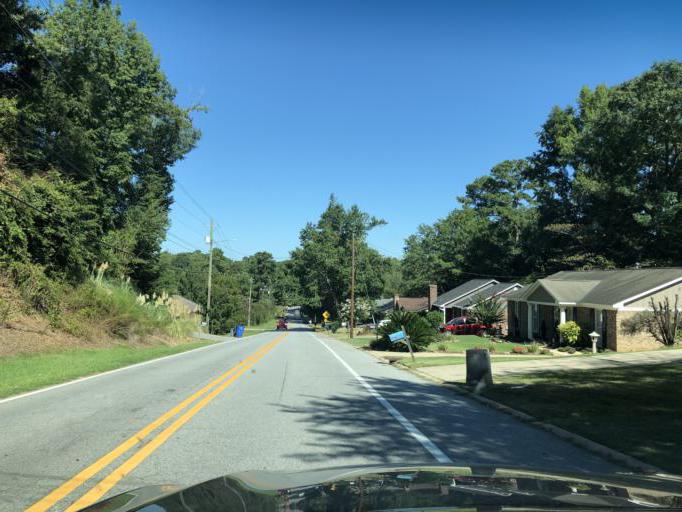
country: US
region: Georgia
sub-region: Muscogee County
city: Columbus
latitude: 32.5068
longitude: -84.9245
